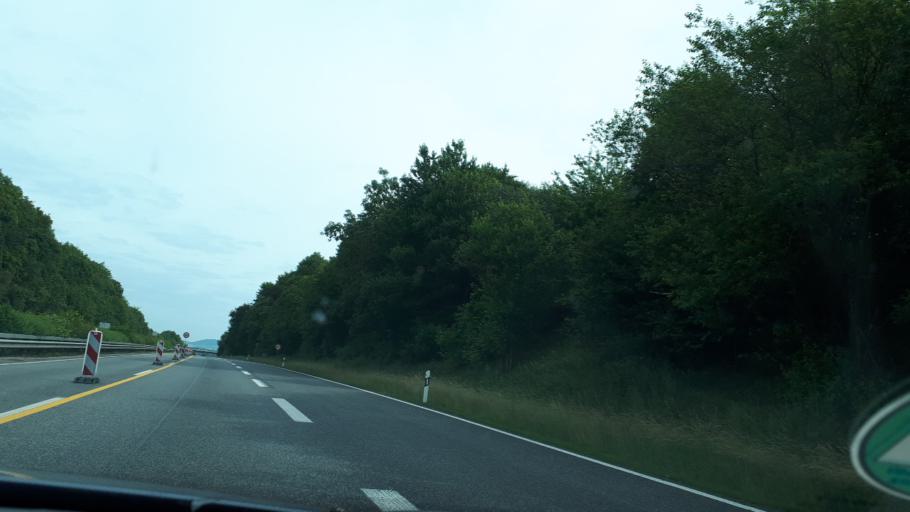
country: DE
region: Rheinland-Pfalz
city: Kaifenheim
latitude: 50.2451
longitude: 7.2168
